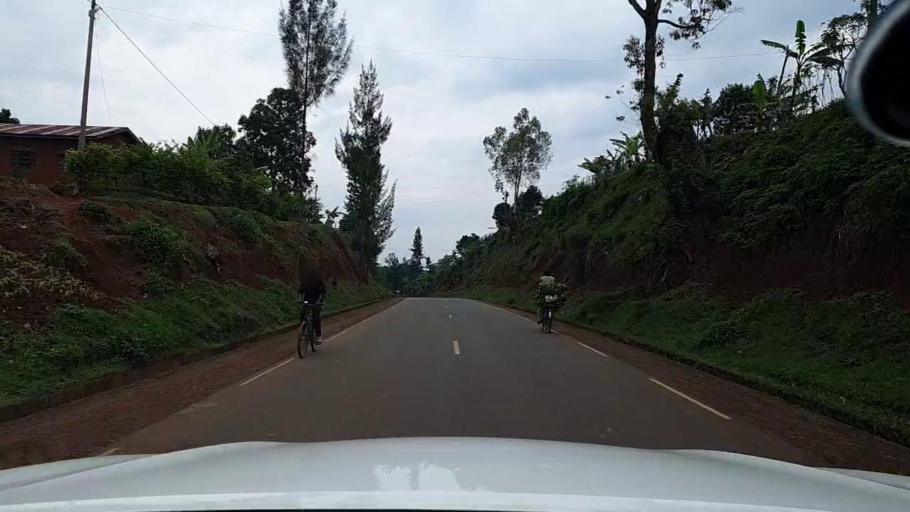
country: RW
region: Western Province
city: Cyangugu
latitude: -2.6096
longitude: 28.9358
